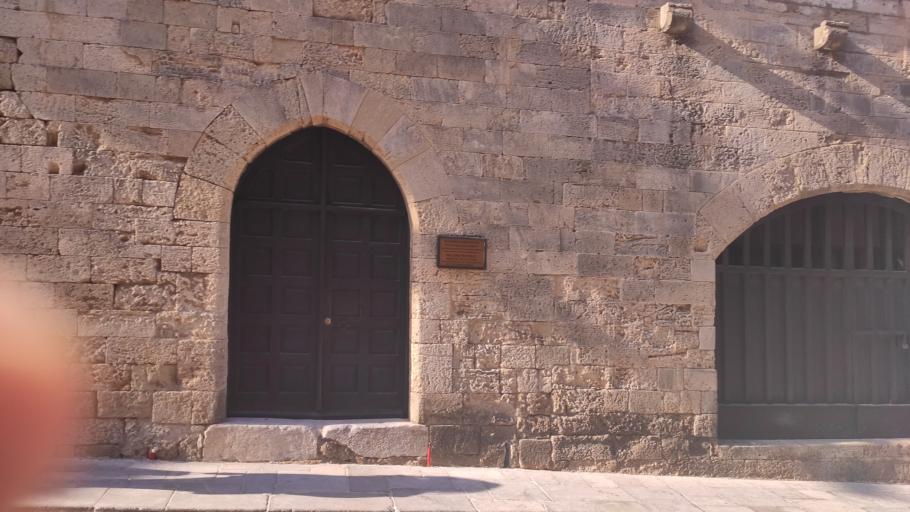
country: GR
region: South Aegean
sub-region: Nomos Dodekanisou
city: Rodos
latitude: 36.4451
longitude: 28.2265
